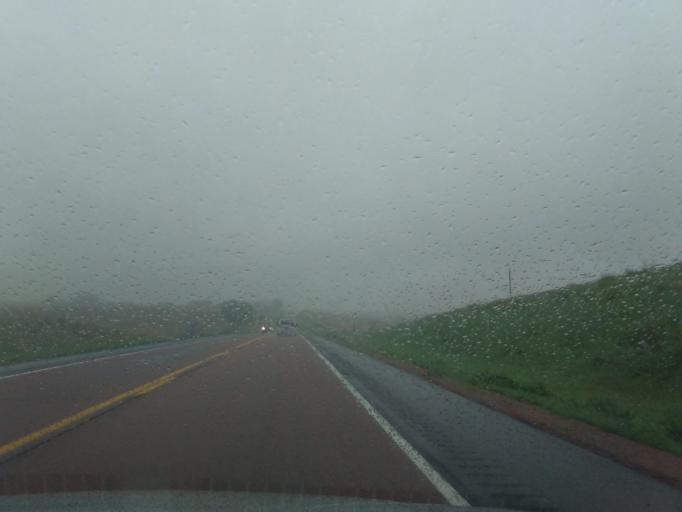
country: US
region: Nebraska
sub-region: Wayne County
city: Wayne
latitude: 42.2356
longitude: -97.1237
